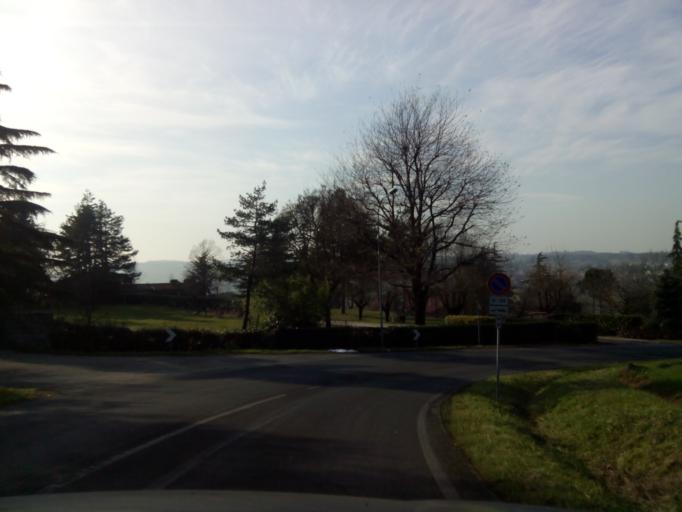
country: IT
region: Emilia-Romagna
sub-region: Provincia di Bologna
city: Imola
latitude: 44.3346
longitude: 11.7015
